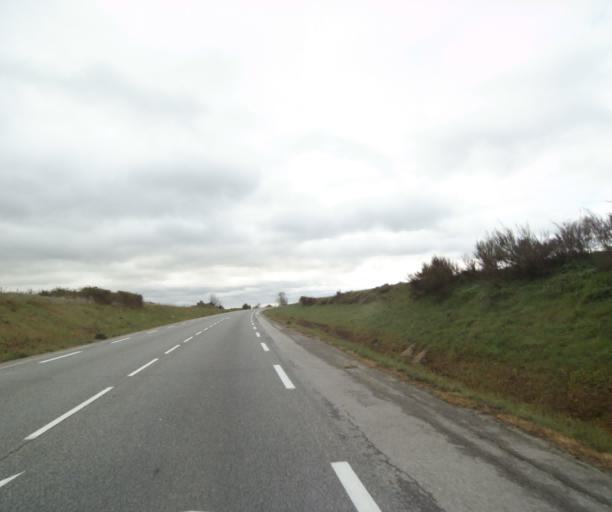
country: FR
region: Midi-Pyrenees
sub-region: Departement de l'Ariege
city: Saverdun
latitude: 43.2348
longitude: 1.5979
